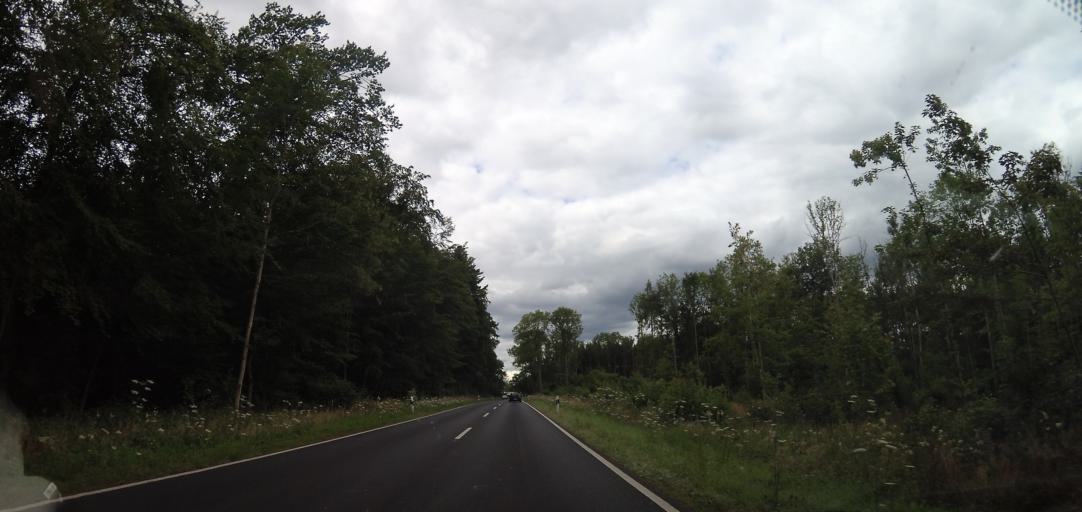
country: DE
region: Rheinland-Pfalz
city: Berndorf
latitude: 50.2851
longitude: 6.6955
